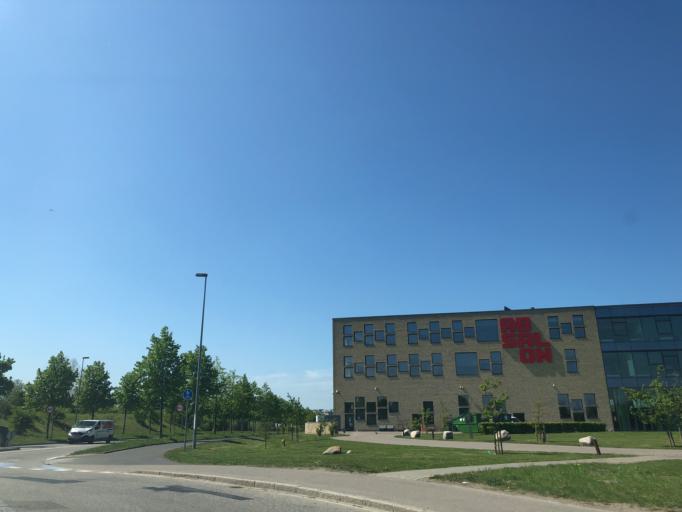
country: DK
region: Zealand
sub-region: Roskilde Kommune
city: Vindinge
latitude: 55.6506
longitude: 12.1441
